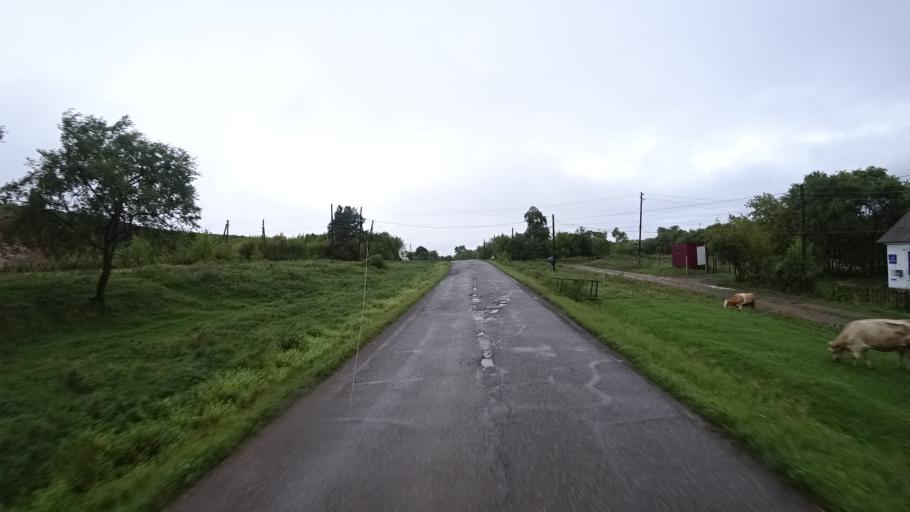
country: RU
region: Primorskiy
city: Monastyrishche
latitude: 44.2637
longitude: 132.4206
